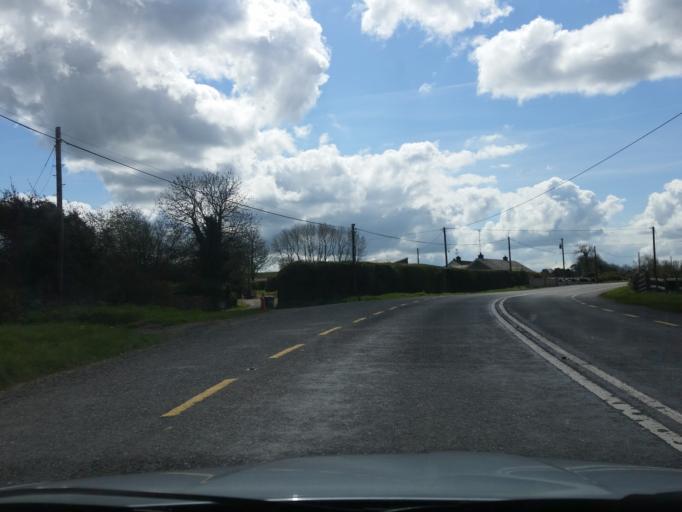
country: IE
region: Leinster
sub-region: An Mhi
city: Slane
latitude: 53.6942
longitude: -6.5387
